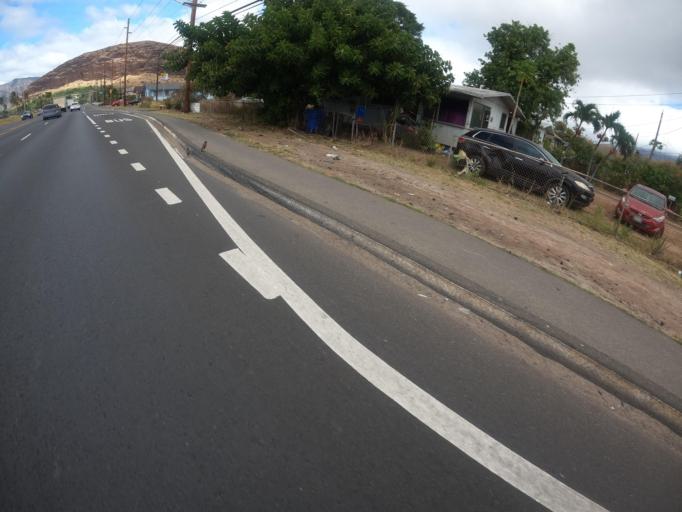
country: US
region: Hawaii
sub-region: Honolulu County
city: Ma'ili
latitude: 21.4213
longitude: -158.1775
